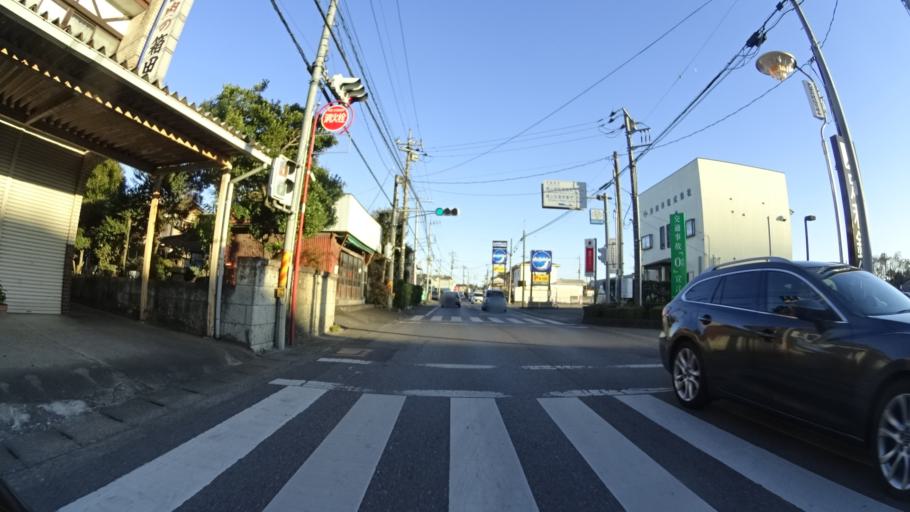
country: JP
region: Tochigi
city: Utsunomiya-shi
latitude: 36.5896
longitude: 139.8264
